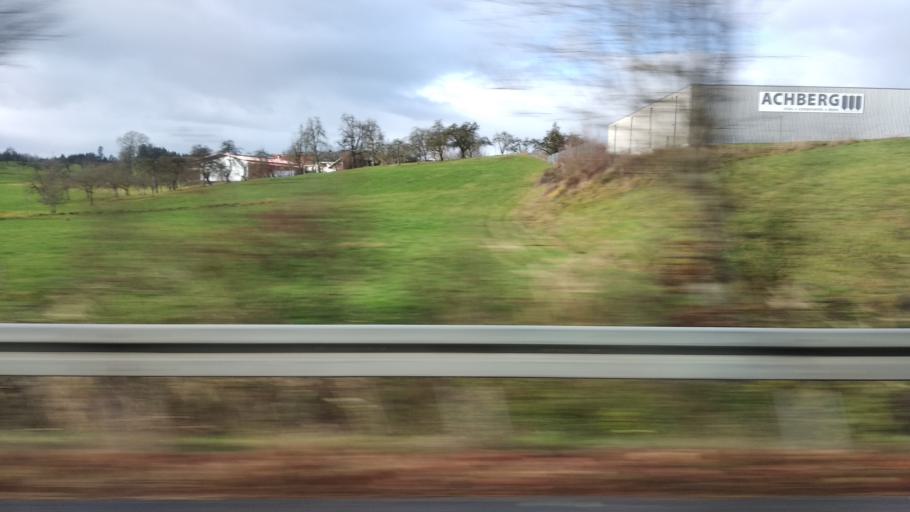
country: DE
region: Bavaria
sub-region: Swabia
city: Hergensweiler
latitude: 47.6286
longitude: 9.7401
